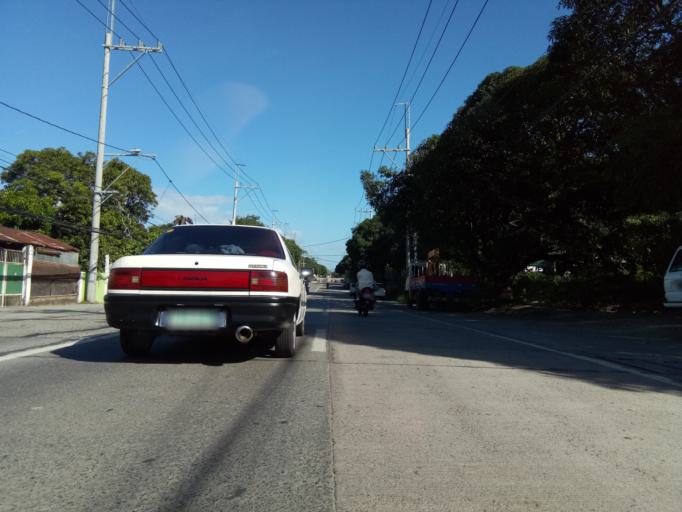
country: PH
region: Calabarzon
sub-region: Province of Cavite
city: Dasmarinas
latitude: 14.3522
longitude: 120.9484
